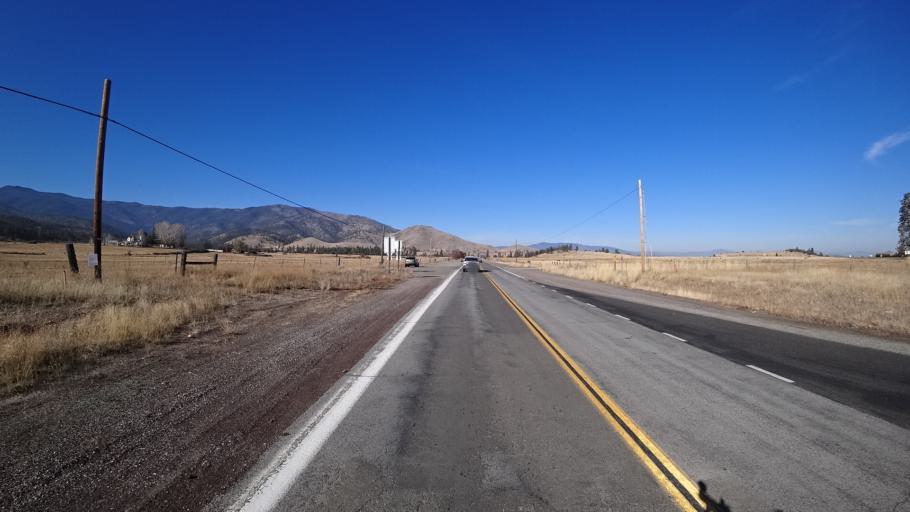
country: US
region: California
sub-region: Siskiyou County
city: Weed
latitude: 41.4413
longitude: -122.4369
